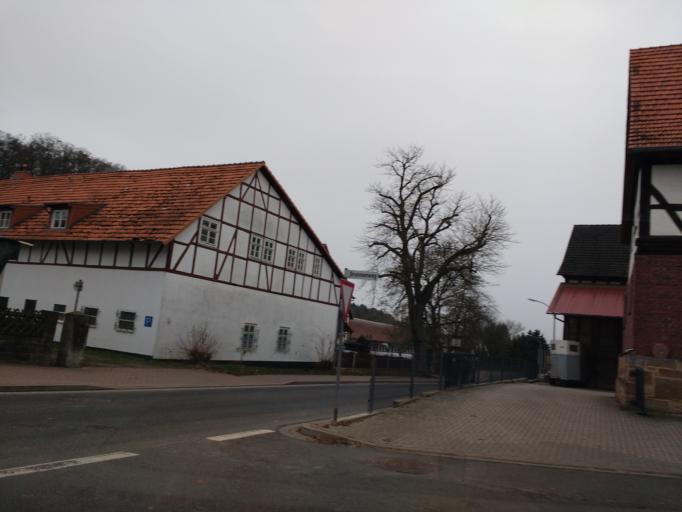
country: DE
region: Hesse
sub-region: Regierungsbezirk Kassel
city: Rotenburg an der Fulda
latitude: 51.0675
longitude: 9.7772
